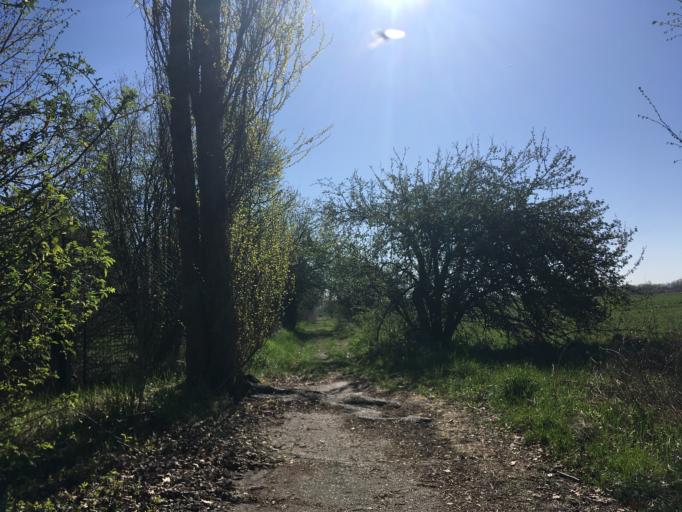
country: DE
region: Berlin
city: Buchholz
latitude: 52.6292
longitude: 13.4444
